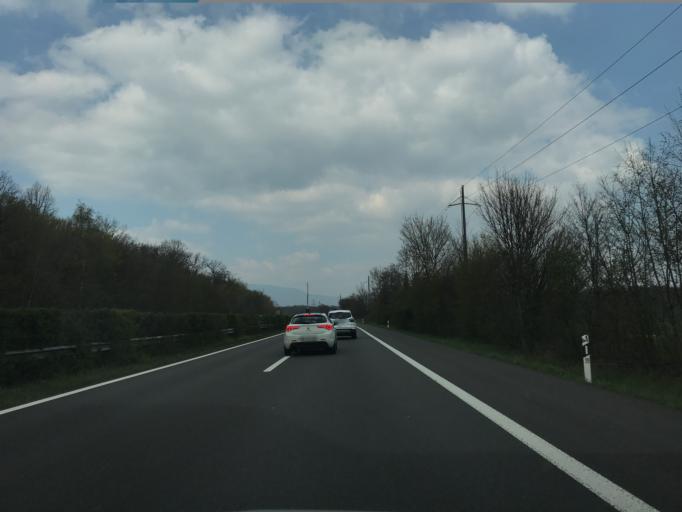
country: CH
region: Geneva
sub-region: Geneva
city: Versoix
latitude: 46.2907
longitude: 6.1463
